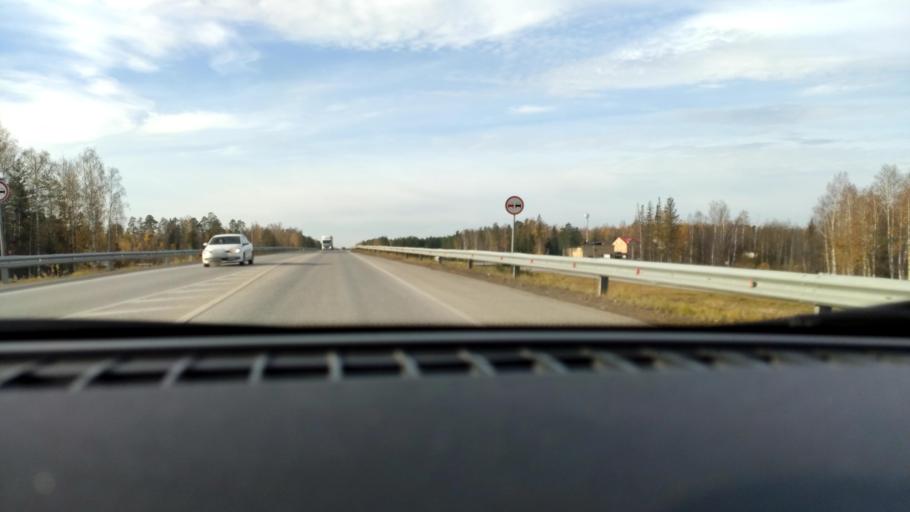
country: RU
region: Perm
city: Overyata
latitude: 58.0447
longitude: 55.8779
